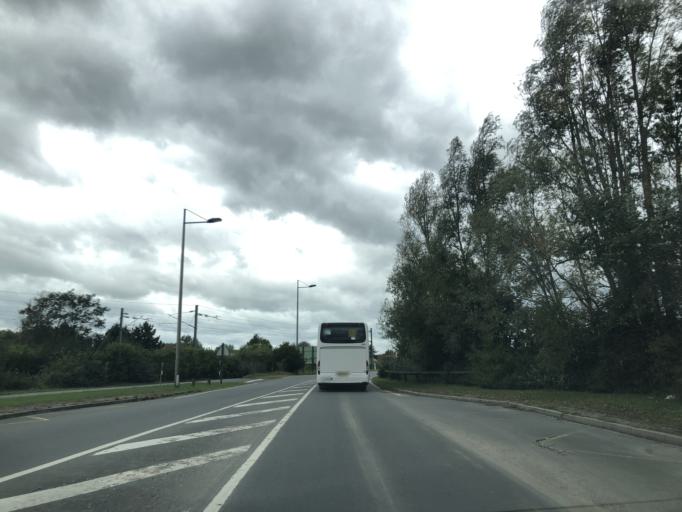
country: FR
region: Nord-Pas-de-Calais
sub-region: Departement du Pas-de-Calais
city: Saint-Josse
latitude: 50.4639
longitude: 1.6486
